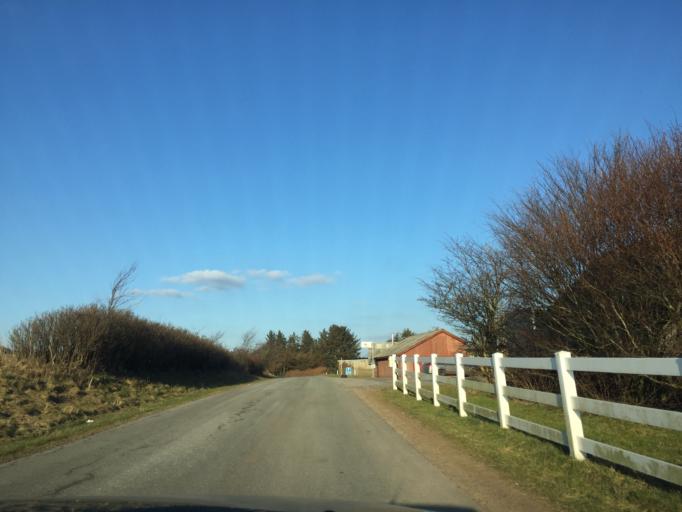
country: DK
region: Central Jutland
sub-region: Holstebro Kommune
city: Vinderup
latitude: 56.5814
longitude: 8.8069
